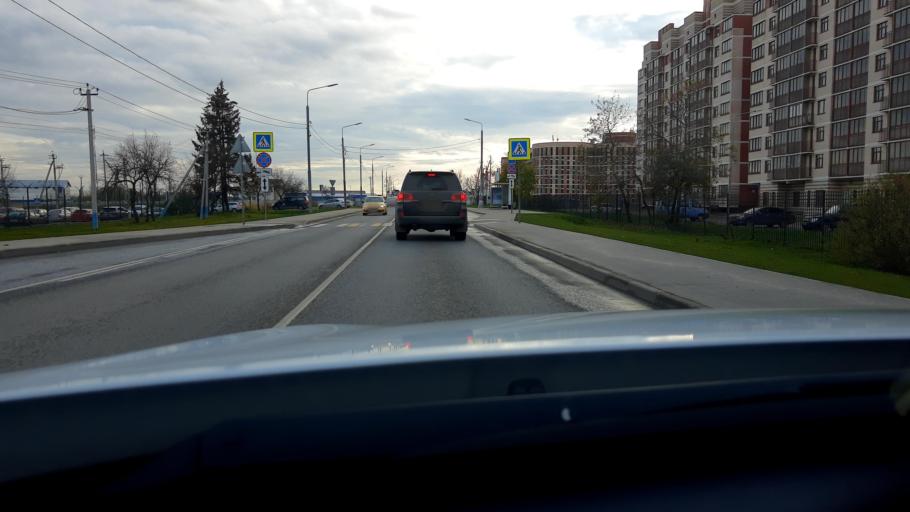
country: RU
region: Moskovskaya
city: Kokoshkino
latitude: 55.5457
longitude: 37.1564
